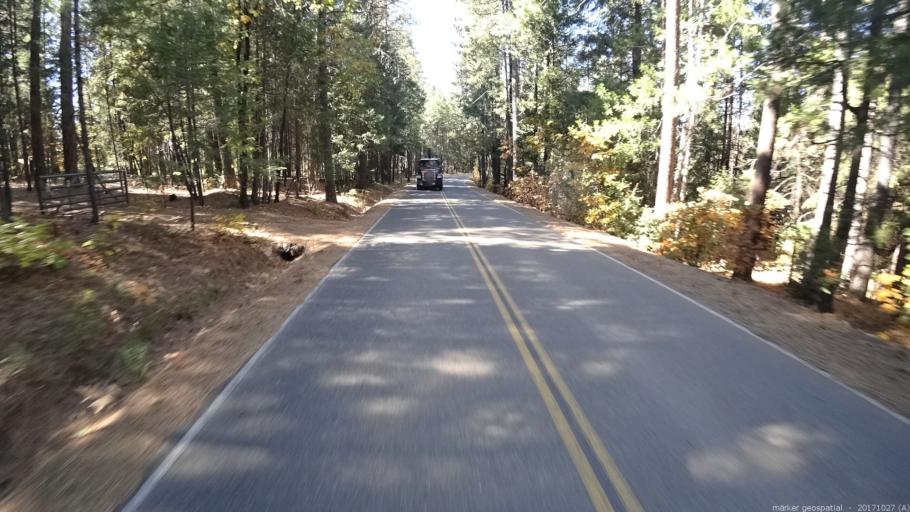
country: US
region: California
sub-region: Shasta County
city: Shingletown
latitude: 40.7112
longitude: -121.9454
